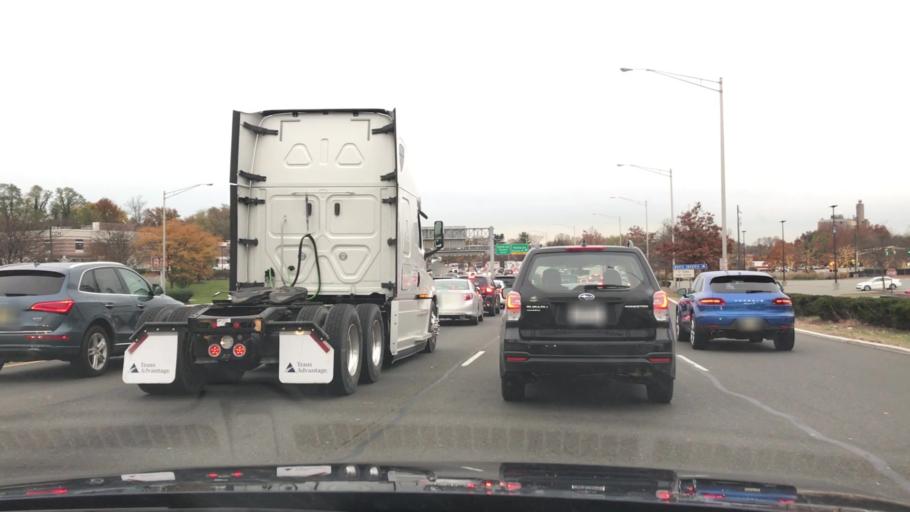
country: US
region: New Jersey
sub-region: Bergen County
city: Rochelle Park
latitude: 40.9184
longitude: -74.0727
